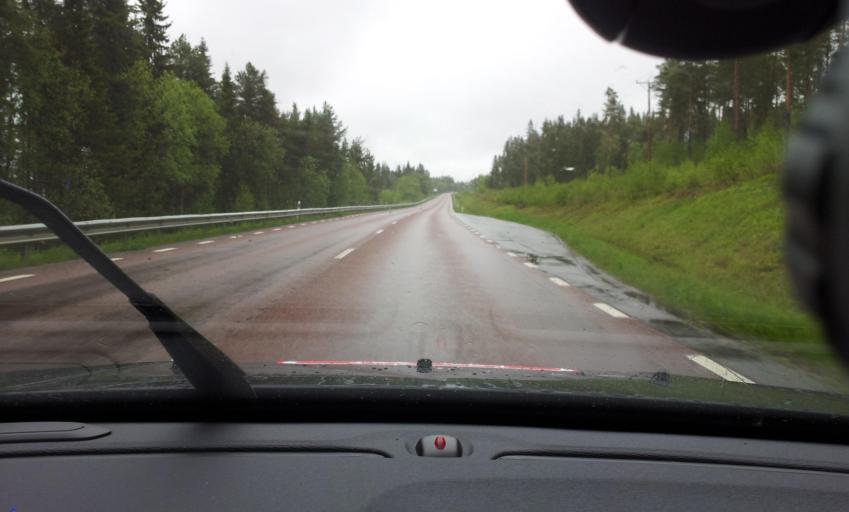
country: SE
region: Jaemtland
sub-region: Bergs Kommun
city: Hoverberg
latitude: 62.7776
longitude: 14.4492
